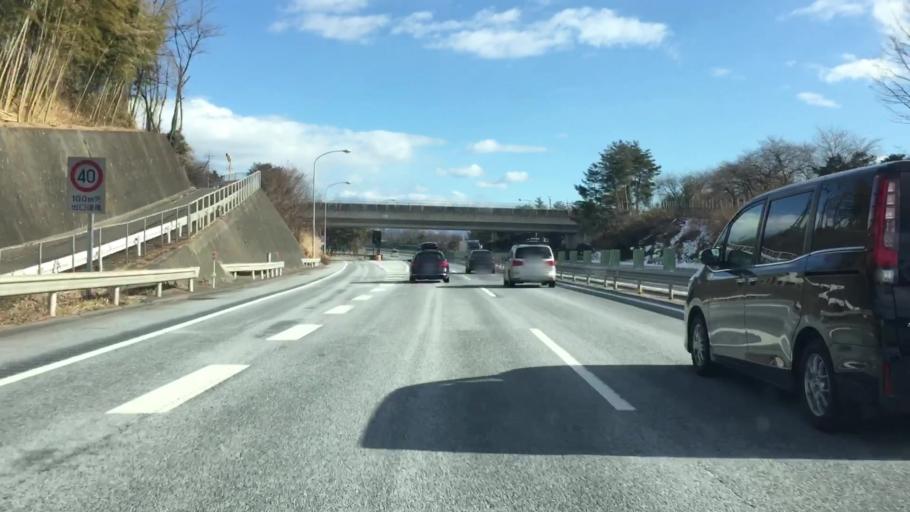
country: JP
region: Gunma
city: Numata
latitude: 36.6772
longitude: 139.0154
